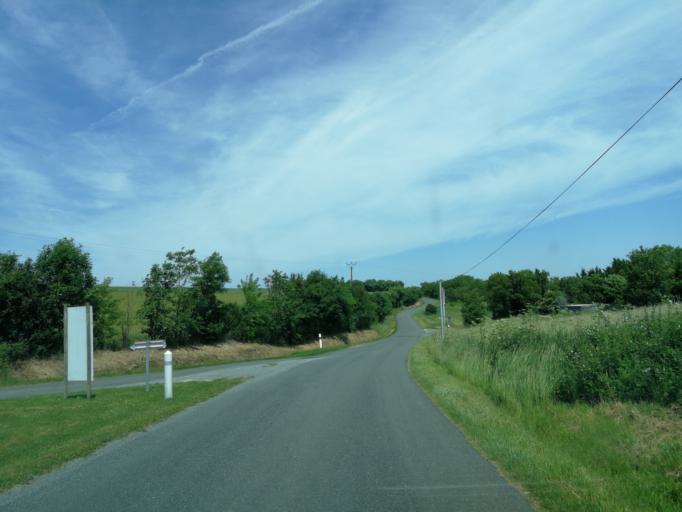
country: FR
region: Pays de la Loire
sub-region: Departement de la Vendee
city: Le Langon
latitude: 46.4261
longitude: -0.8934
